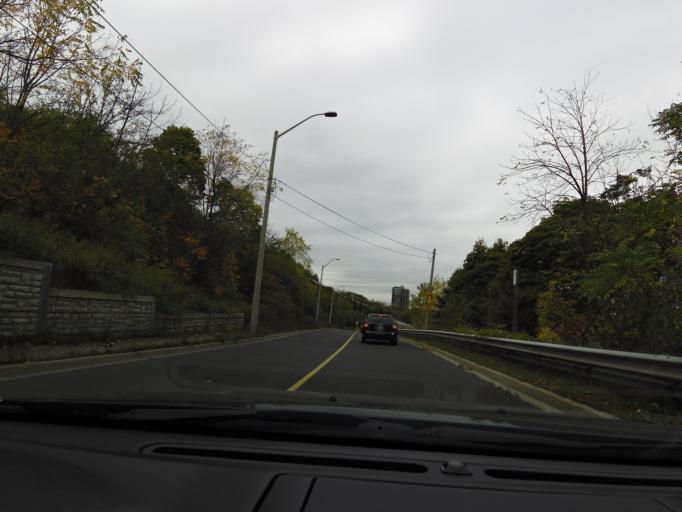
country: CA
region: Ontario
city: Hamilton
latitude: 43.2455
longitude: -79.8593
